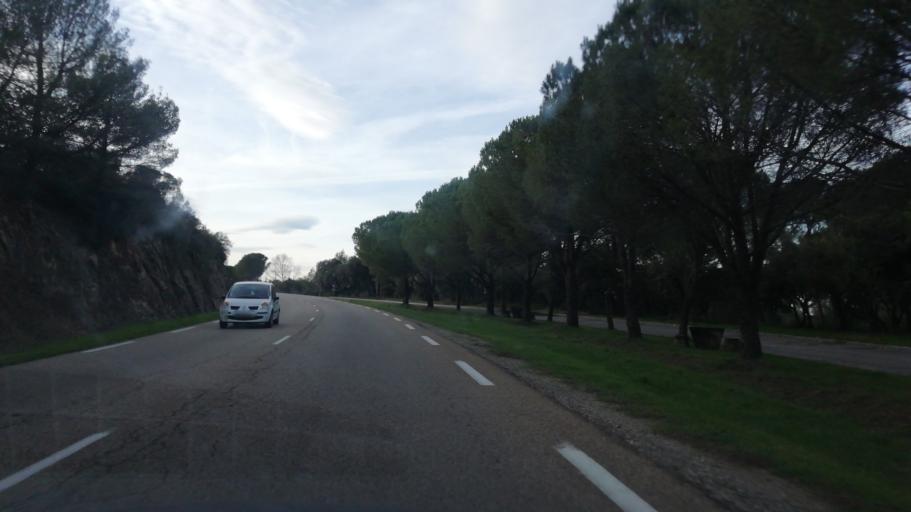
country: FR
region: Languedoc-Roussillon
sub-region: Departement du Gard
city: Caveirac
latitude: 43.8507
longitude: 4.2835
